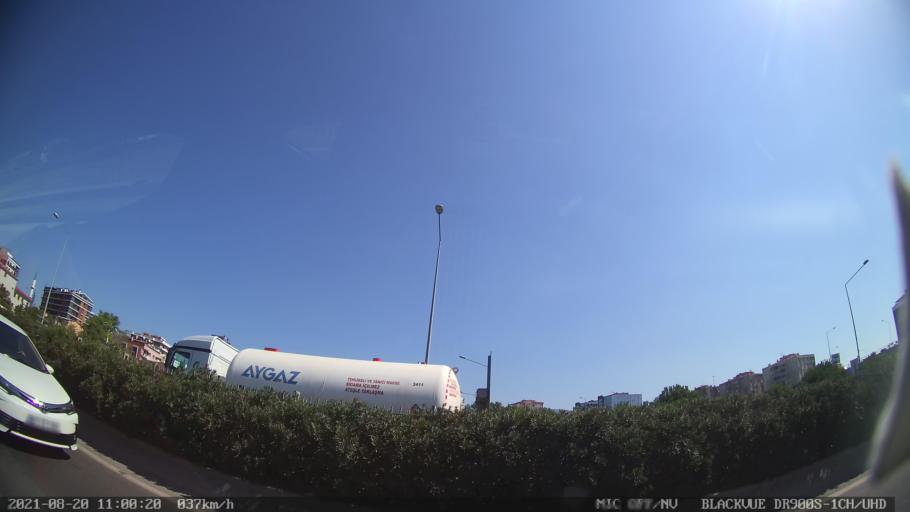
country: TR
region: Izmir
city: Karsiyaka
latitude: 38.4705
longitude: 27.1105
